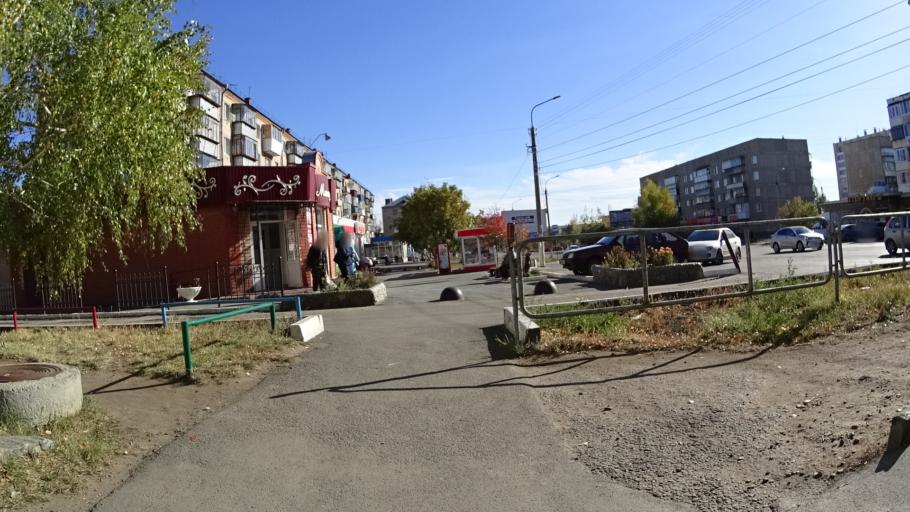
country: RU
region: Chelyabinsk
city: Troitsk
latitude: 54.0795
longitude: 61.5295
